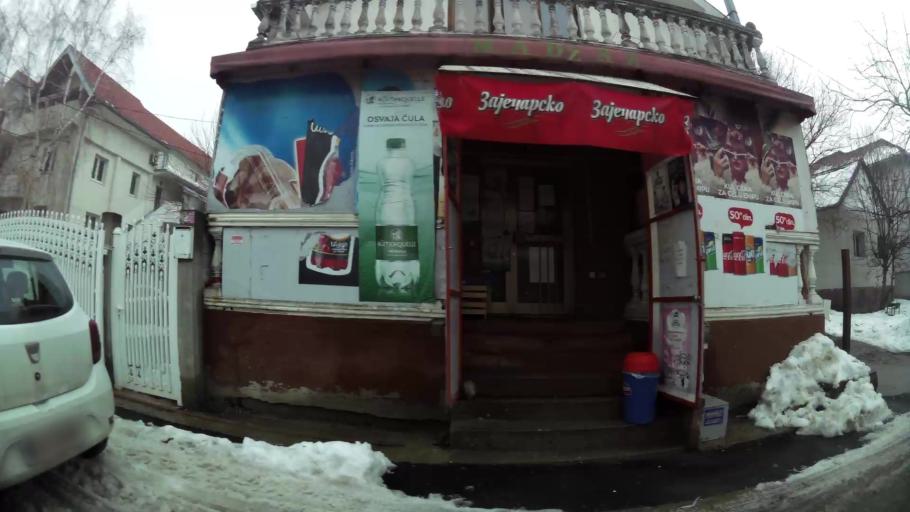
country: RS
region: Central Serbia
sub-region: Belgrade
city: Zvezdara
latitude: 44.7745
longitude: 20.5312
